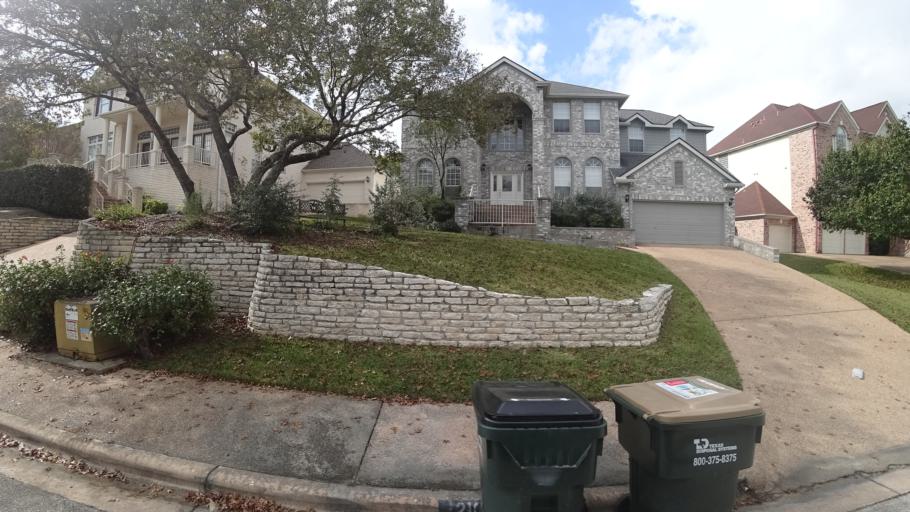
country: US
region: Texas
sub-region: Travis County
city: Barton Creek
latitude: 30.3027
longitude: -97.8895
